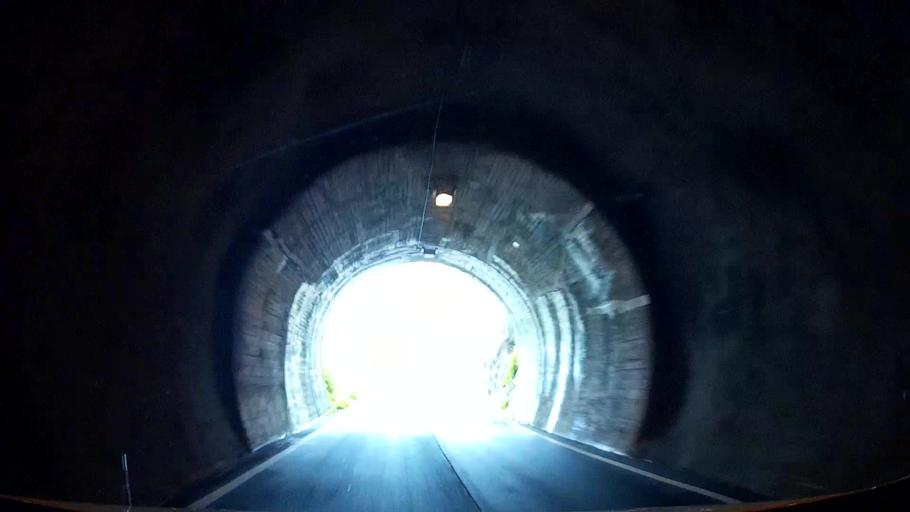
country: JP
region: Shizuoka
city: Shimoda
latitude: 34.6121
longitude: 138.8269
